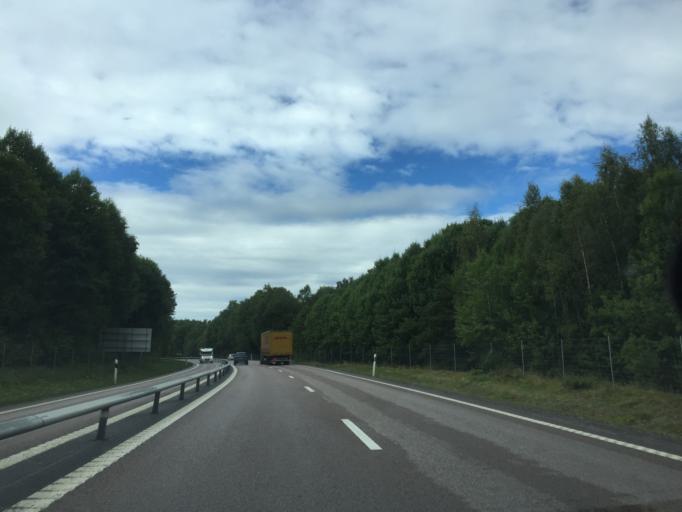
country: SE
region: Vaestmanland
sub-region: Kungsors Kommun
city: Kungsoer
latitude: 59.4186
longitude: 16.0614
